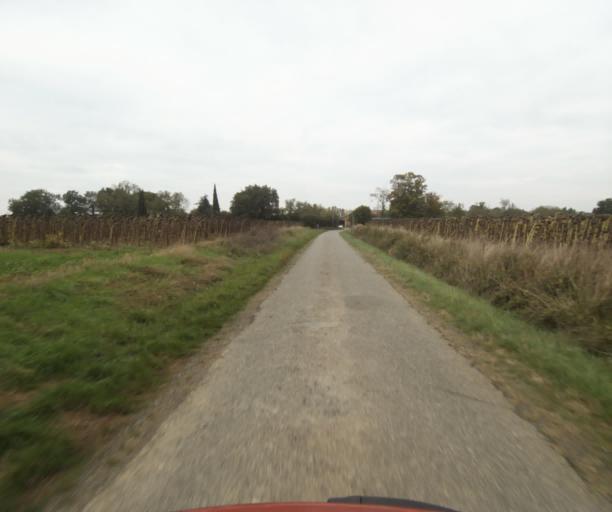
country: FR
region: Midi-Pyrenees
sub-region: Departement du Tarn-et-Garonne
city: Verdun-sur-Garonne
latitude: 43.8204
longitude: 1.2071
